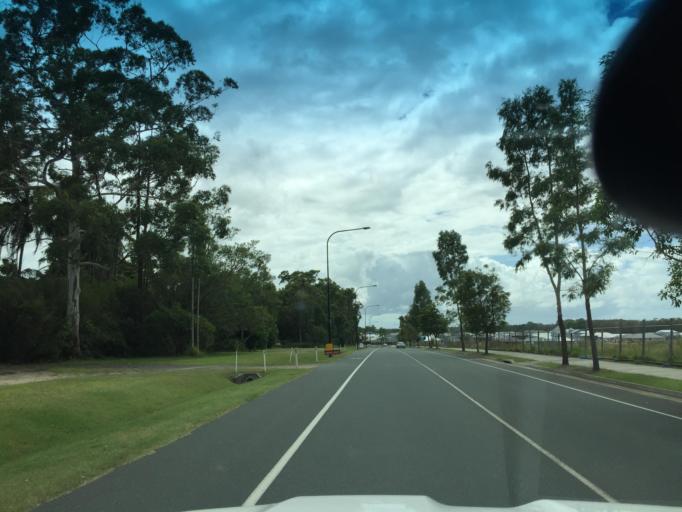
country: AU
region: Queensland
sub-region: Moreton Bay
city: Morayfield
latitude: -27.1264
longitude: 152.9912
